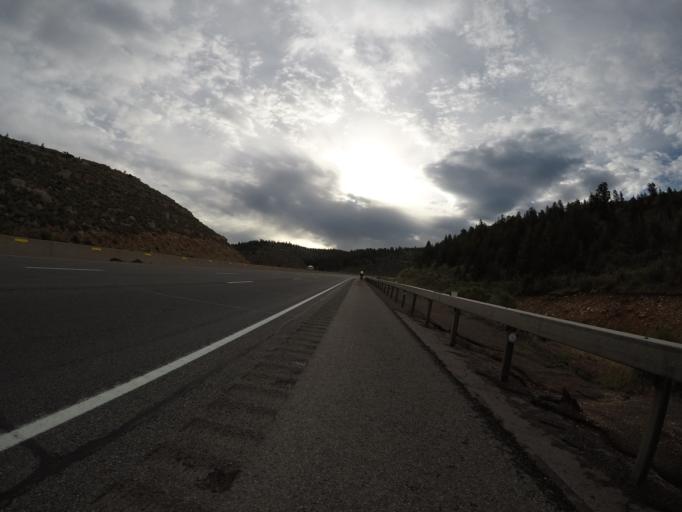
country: US
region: Wyoming
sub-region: Albany County
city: Laramie
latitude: 41.2720
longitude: -105.4877
